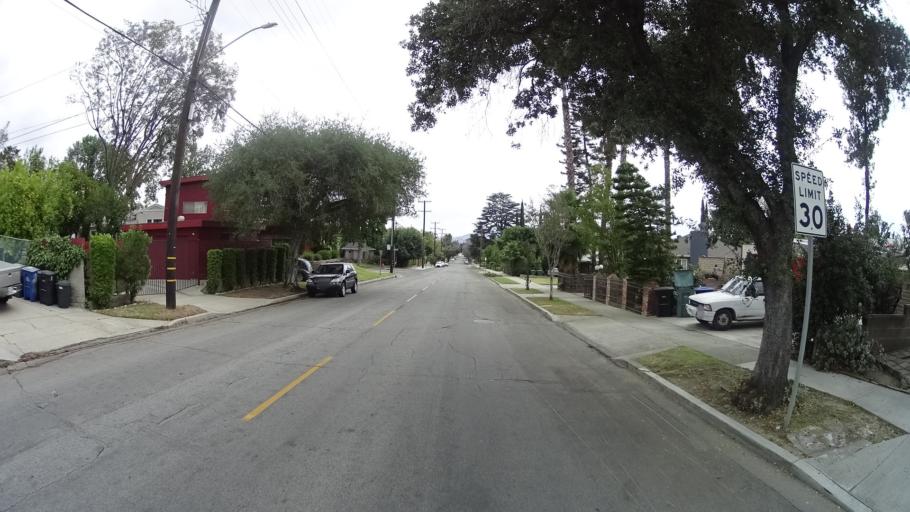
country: US
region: California
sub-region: Los Angeles County
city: Burbank
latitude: 34.2024
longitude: -118.3278
